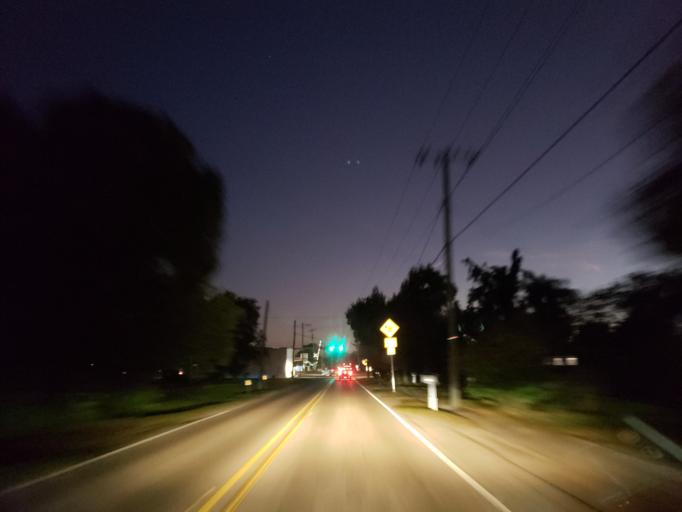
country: US
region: Florida
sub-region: Hillsborough County
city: Dover
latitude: 27.9955
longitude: -82.2197
